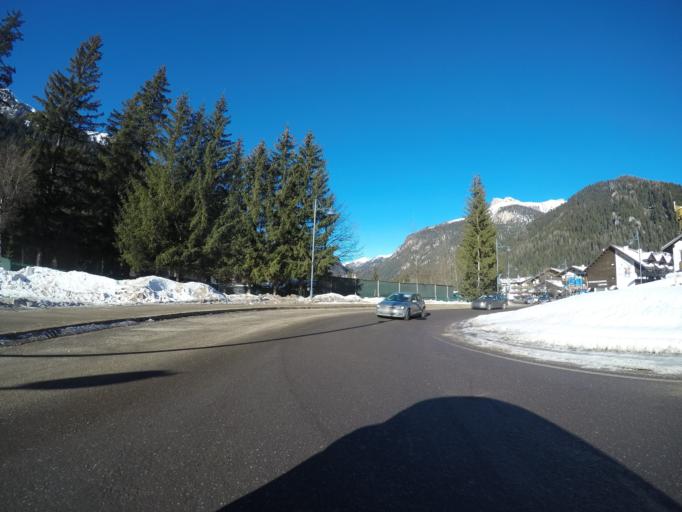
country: IT
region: Trentino-Alto Adige
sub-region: Provincia di Trento
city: Canazei
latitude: 46.4723
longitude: 11.7770
